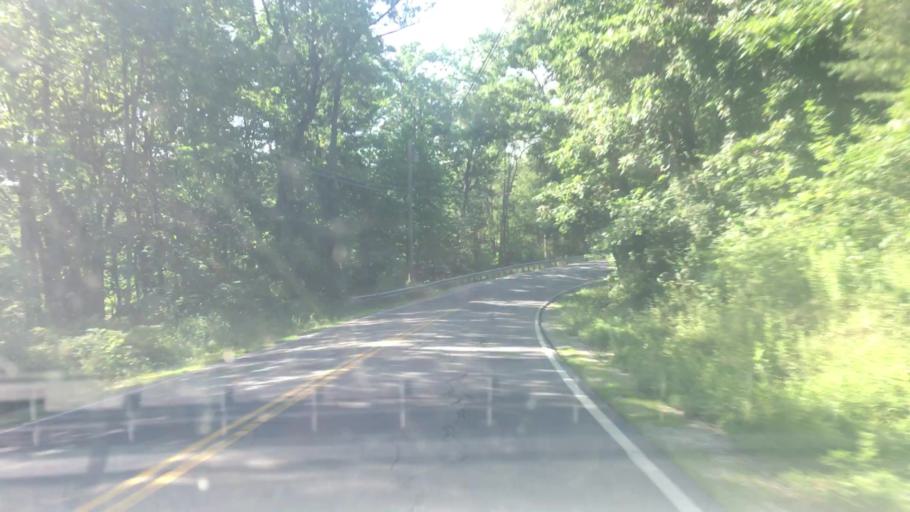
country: US
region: Maine
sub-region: York County
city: Hollis Center
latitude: 43.6504
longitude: -70.5951
